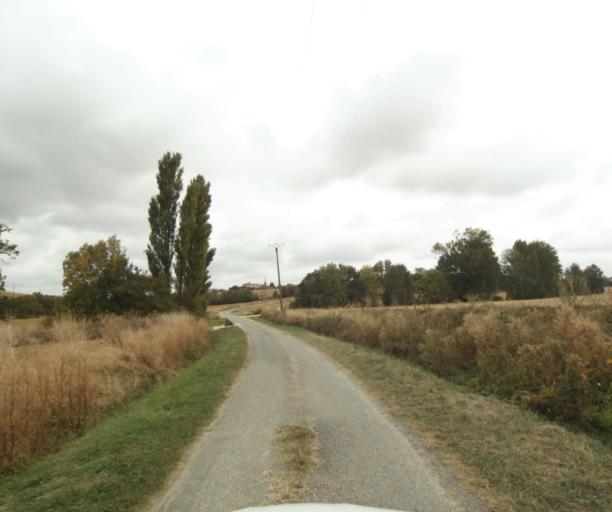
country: FR
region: Midi-Pyrenees
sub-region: Departement de la Haute-Garonne
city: Villefranche-de-Lauragais
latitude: 43.4167
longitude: 1.7315
